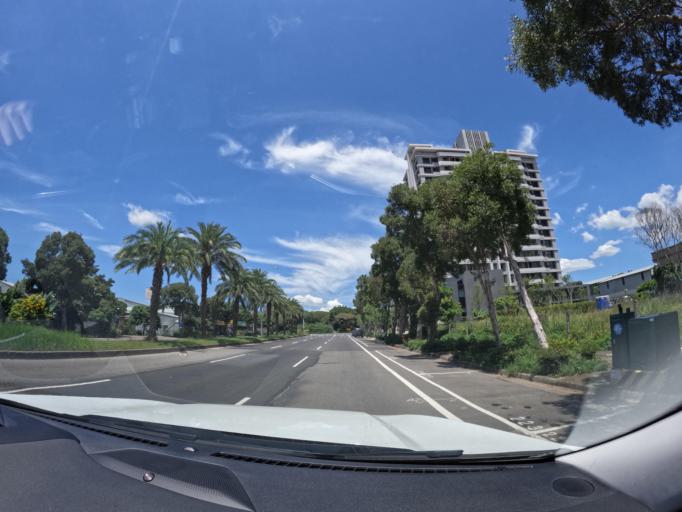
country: TW
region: Taipei
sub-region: Taipei
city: Banqiao
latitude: 25.0931
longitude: 121.3784
